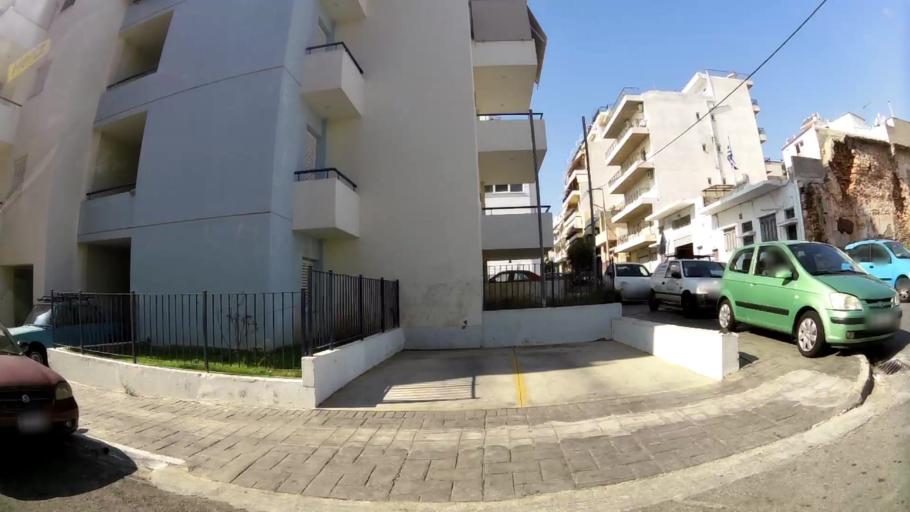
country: GR
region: Attica
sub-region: Nomos Attikis
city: Piraeus
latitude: 37.9503
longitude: 23.6326
